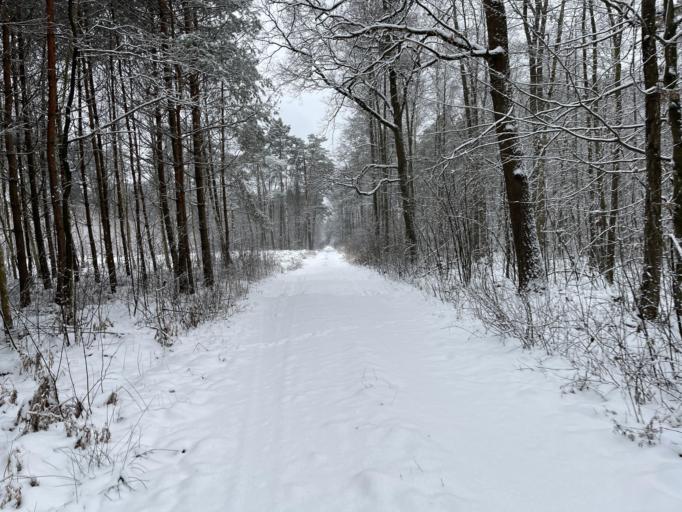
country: PL
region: Masovian Voivodeship
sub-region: Powiat zyrardowski
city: Mrozy
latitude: 52.0362
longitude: 20.2724
